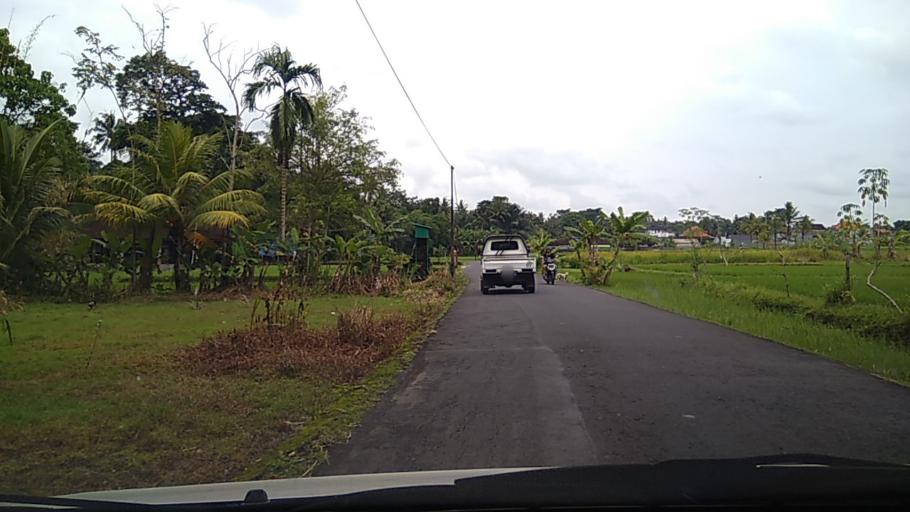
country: ID
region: Bali
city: Banjar Sempidi
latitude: -8.5218
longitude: 115.2125
